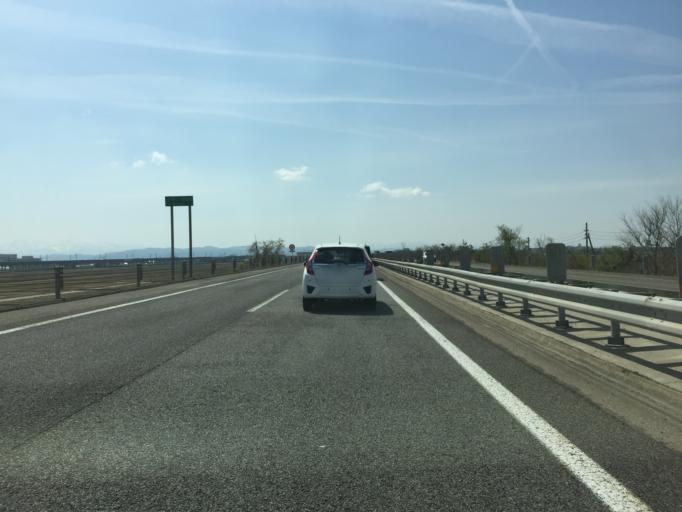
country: JP
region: Niigata
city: Tsubame
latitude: 37.6750
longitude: 138.9441
